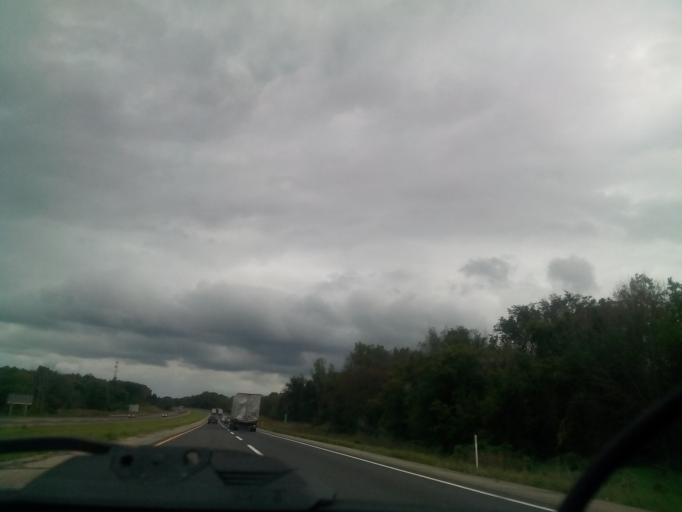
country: US
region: Indiana
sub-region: Steuben County
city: Fremont
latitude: 41.6547
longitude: -84.8441
